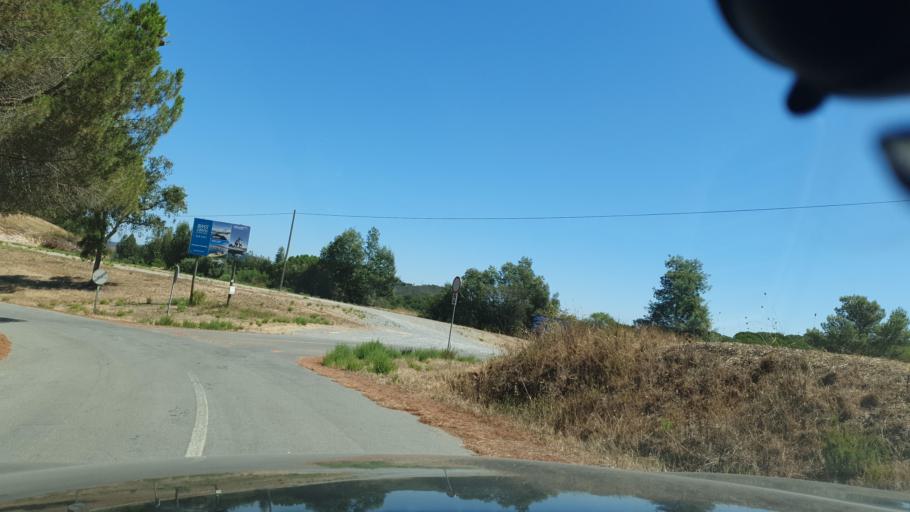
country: PT
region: Faro
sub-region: Monchique
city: Monchique
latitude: 37.5059
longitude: -8.4362
